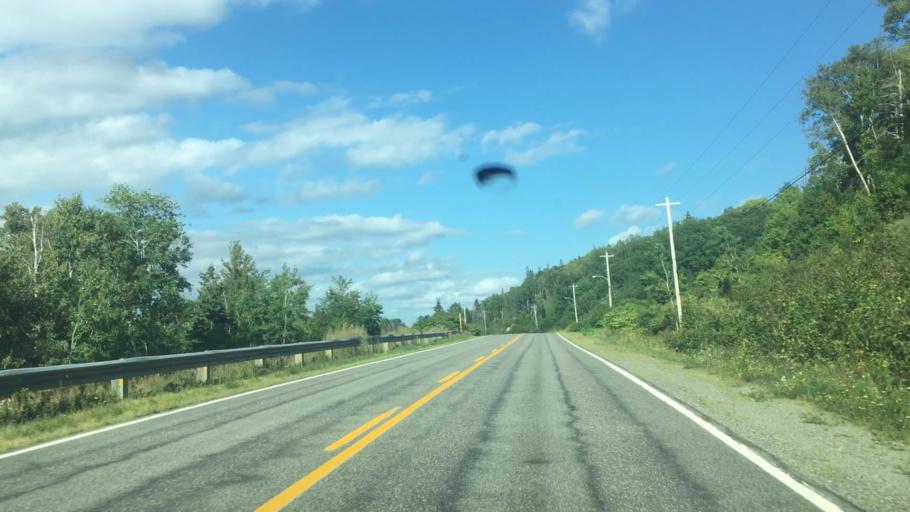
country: CA
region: Nova Scotia
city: Sydney
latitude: 45.8705
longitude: -60.6088
